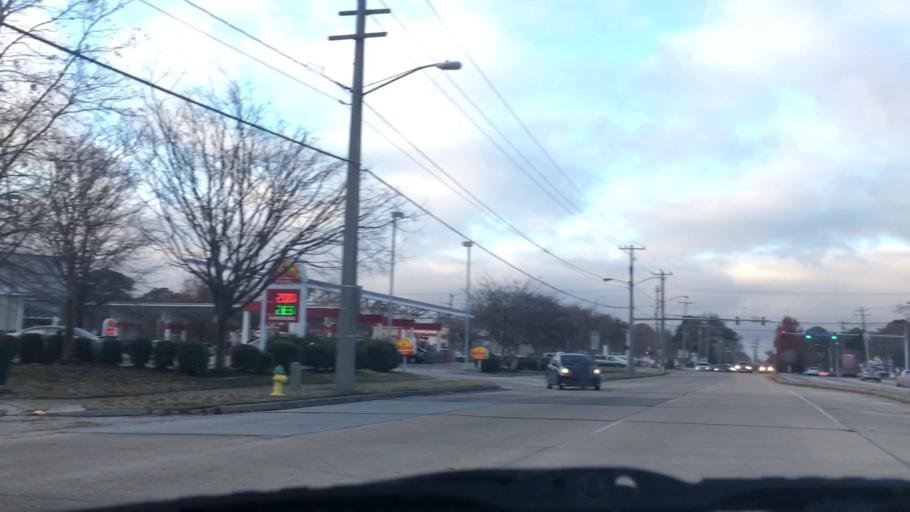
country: US
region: Virginia
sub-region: City of Norfolk
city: Norfolk
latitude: 36.9136
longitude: -76.2414
